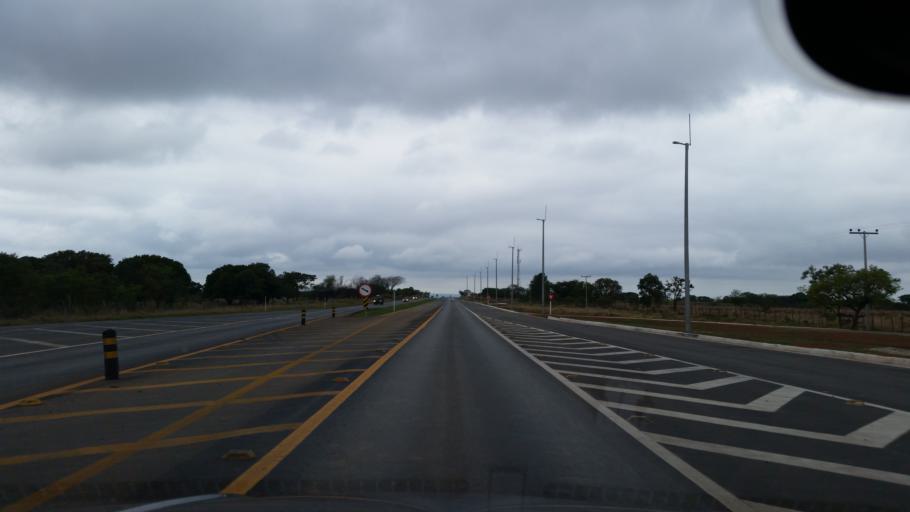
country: BR
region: Goias
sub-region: Luziania
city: Luziania
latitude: -16.4555
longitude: -47.8077
